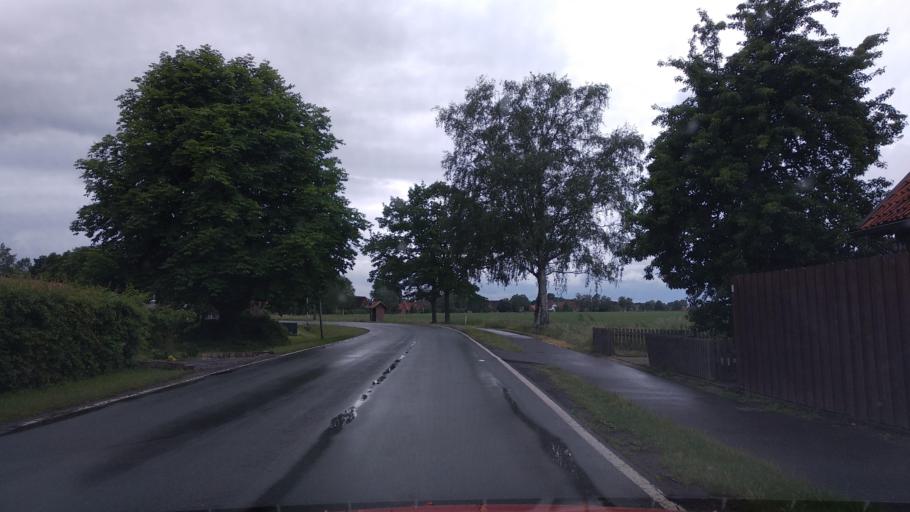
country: DE
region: Lower Saxony
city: Auhagen
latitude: 52.3997
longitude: 9.3045
